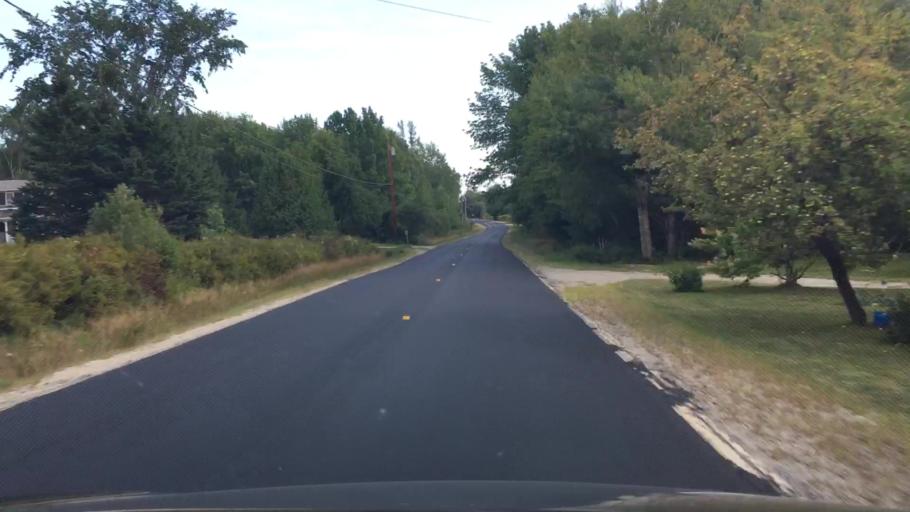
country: US
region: Maine
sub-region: Hancock County
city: Orland
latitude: 44.5507
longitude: -68.6211
